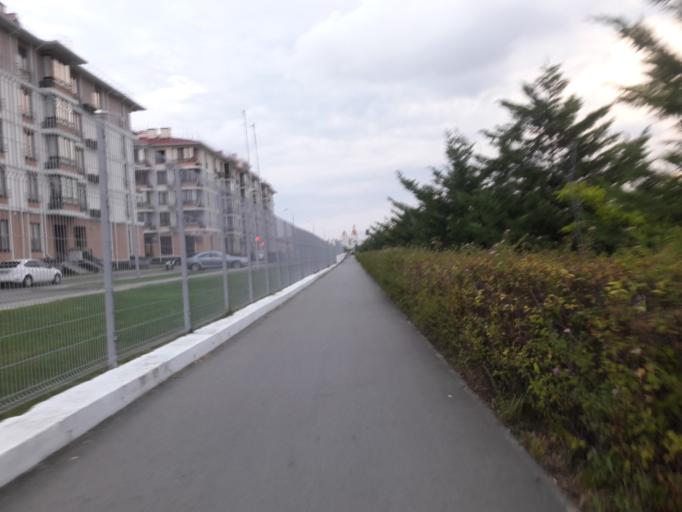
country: RU
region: Krasnodarskiy
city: Adler
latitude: 43.3971
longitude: 39.9783
